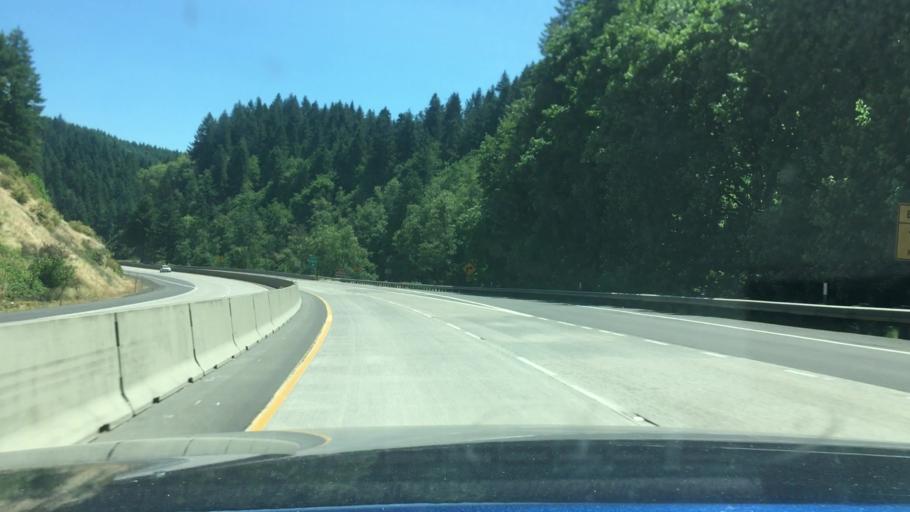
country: US
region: Oregon
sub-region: Douglas County
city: Yoncalla
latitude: 43.6858
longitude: -123.2002
